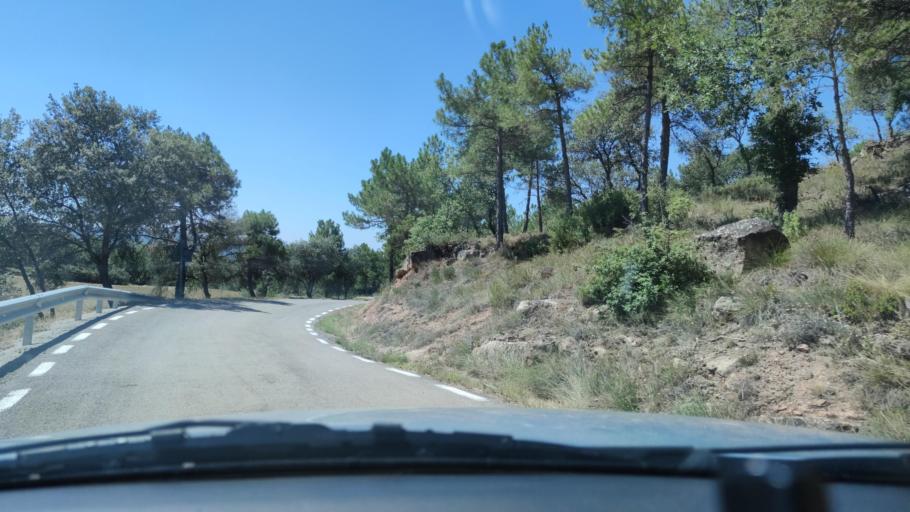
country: ES
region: Catalonia
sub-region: Provincia de Lleida
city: Tora de Riubregos
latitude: 41.8555
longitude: 1.4294
